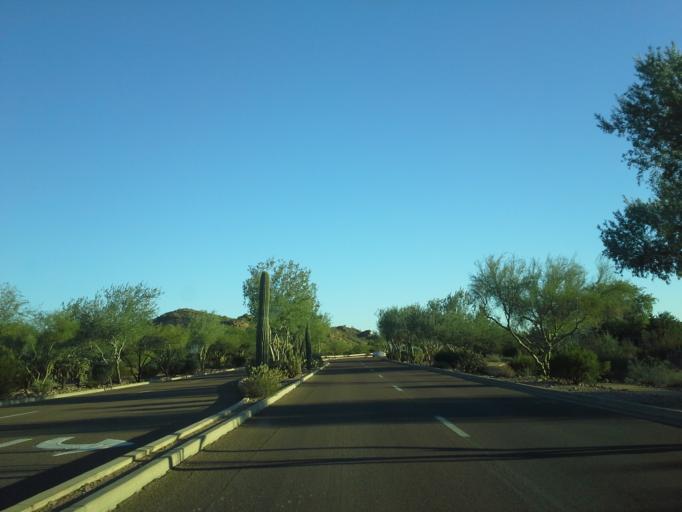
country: US
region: Arizona
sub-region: Pinal County
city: Apache Junction
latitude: 33.3764
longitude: -111.4693
